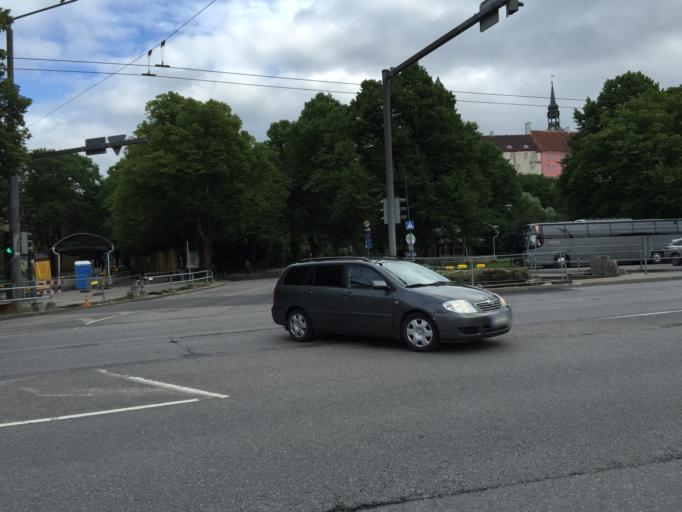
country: EE
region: Harju
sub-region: Tallinna linn
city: Tallinn
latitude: 59.4402
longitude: 24.7392
